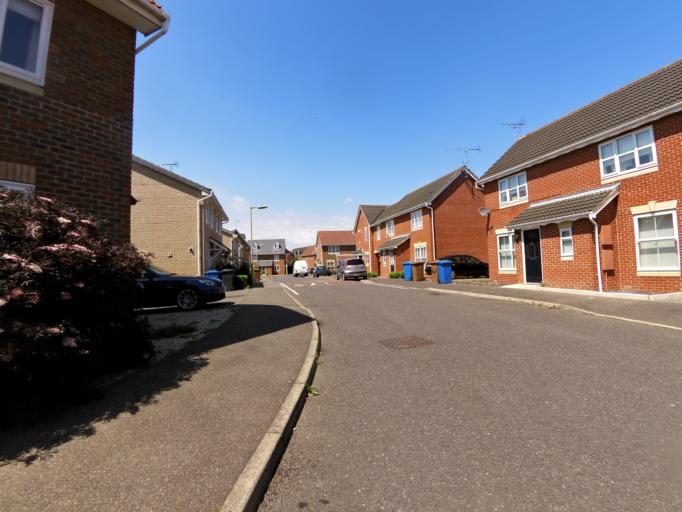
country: GB
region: England
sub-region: Suffolk
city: Ipswich
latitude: 52.0625
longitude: 1.1331
